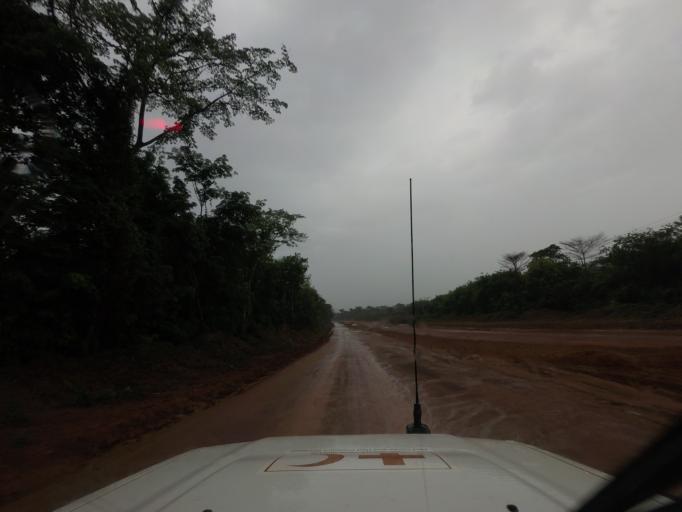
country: LR
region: Nimba
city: Sanniquellie
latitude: 7.2470
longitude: -8.8627
